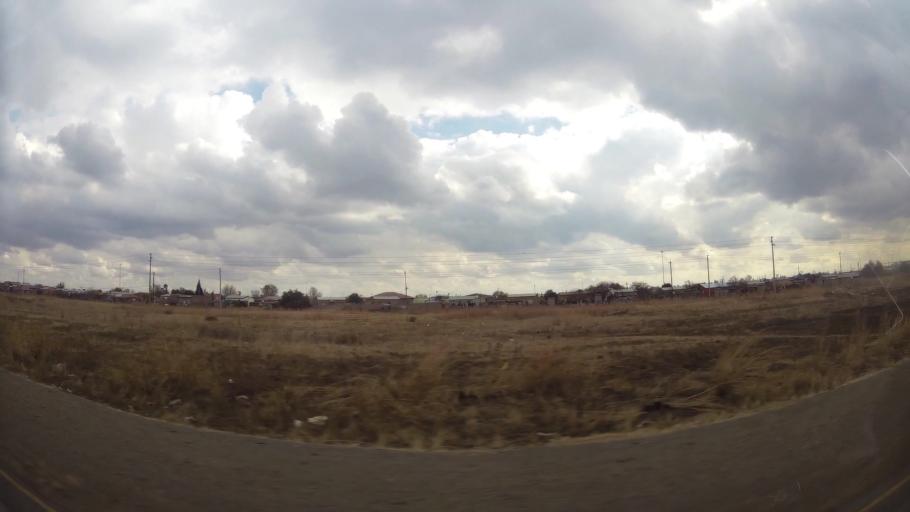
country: ZA
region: Orange Free State
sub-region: Fezile Dabi District Municipality
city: Sasolburg
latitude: -26.8577
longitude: 27.8882
